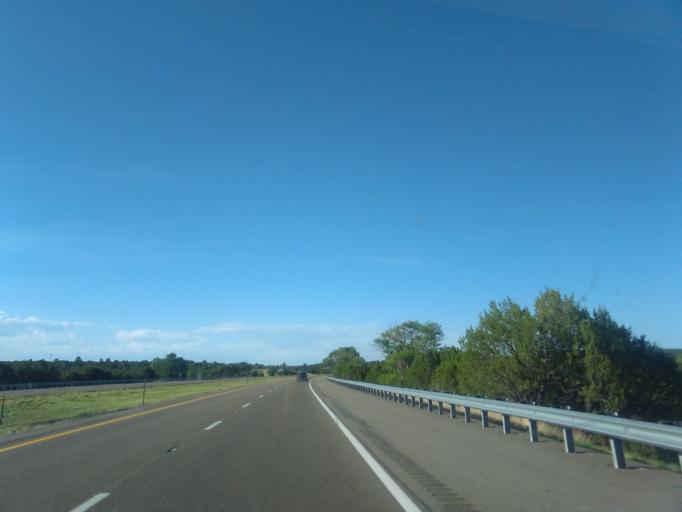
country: US
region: New Mexico
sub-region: San Miguel County
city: Las Vegas
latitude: 35.4806
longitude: -105.2739
